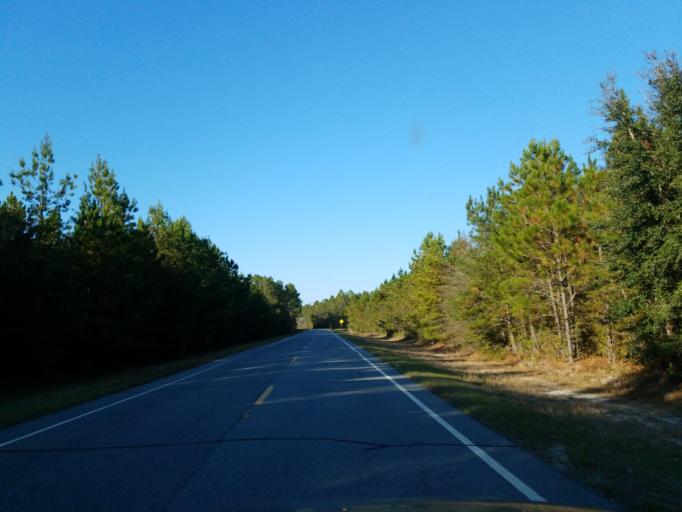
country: US
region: Georgia
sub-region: Echols County
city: Statenville
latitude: 30.8578
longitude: -83.0520
